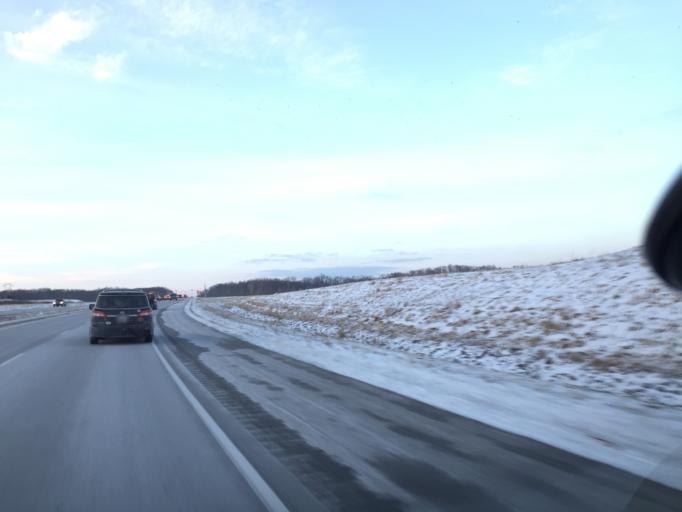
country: US
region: Indiana
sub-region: Monroe County
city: Bloomington
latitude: 39.1898
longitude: -86.5687
